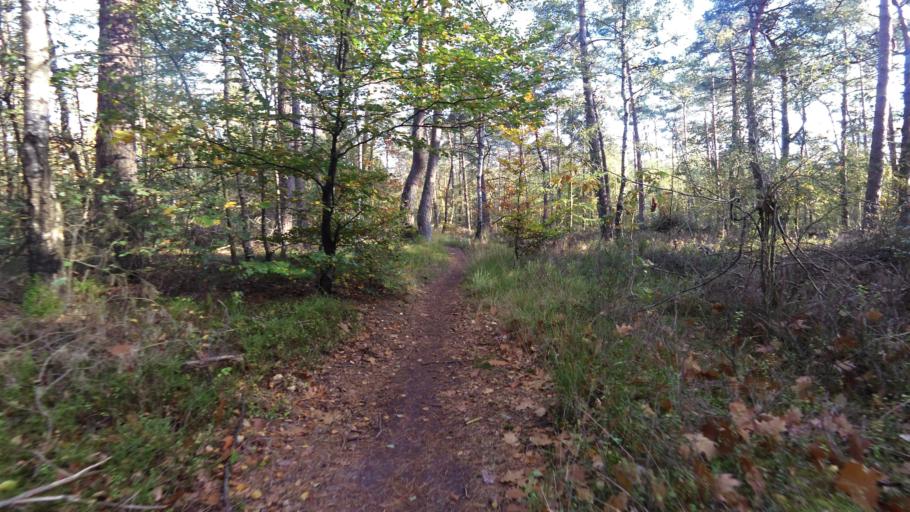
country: NL
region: Gelderland
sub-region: Gemeente Epe
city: Epe
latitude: 52.3951
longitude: 5.9920
